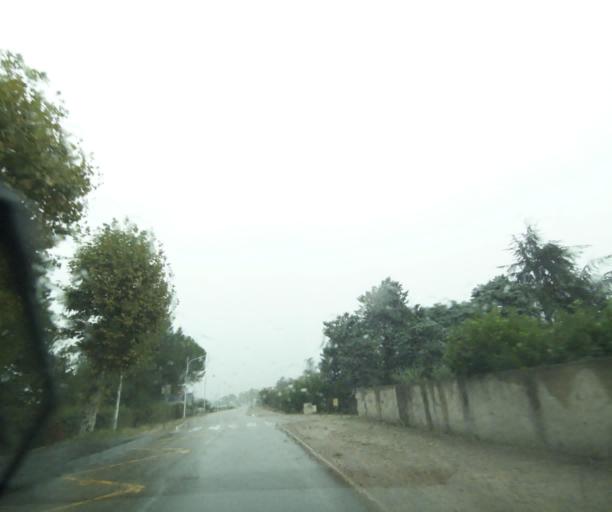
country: FR
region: Languedoc-Roussillon
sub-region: Departement du Gard
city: Milhaud
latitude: 43.7967
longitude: 4.3135
